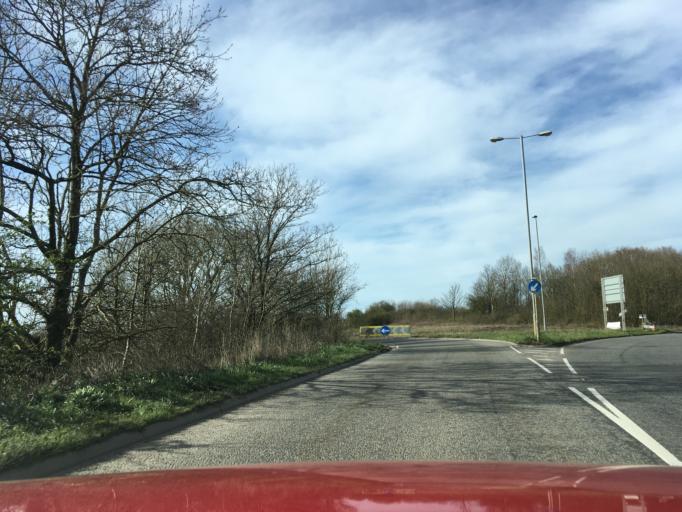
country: GB
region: England
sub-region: Wiltshire
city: Chippenham
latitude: 51.5135
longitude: -2.1207
